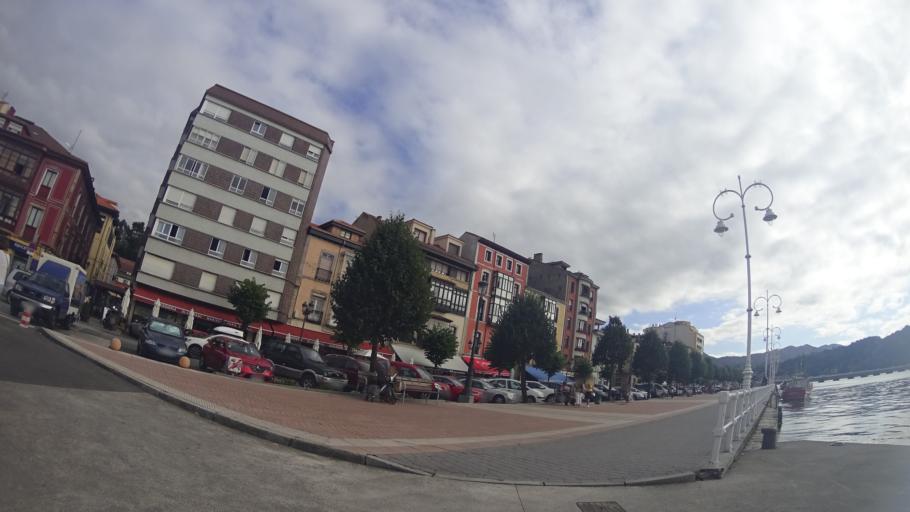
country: ES
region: Asturias
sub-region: Province of Asturias
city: Ribadesella
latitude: 43.4634
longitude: -5.0587
